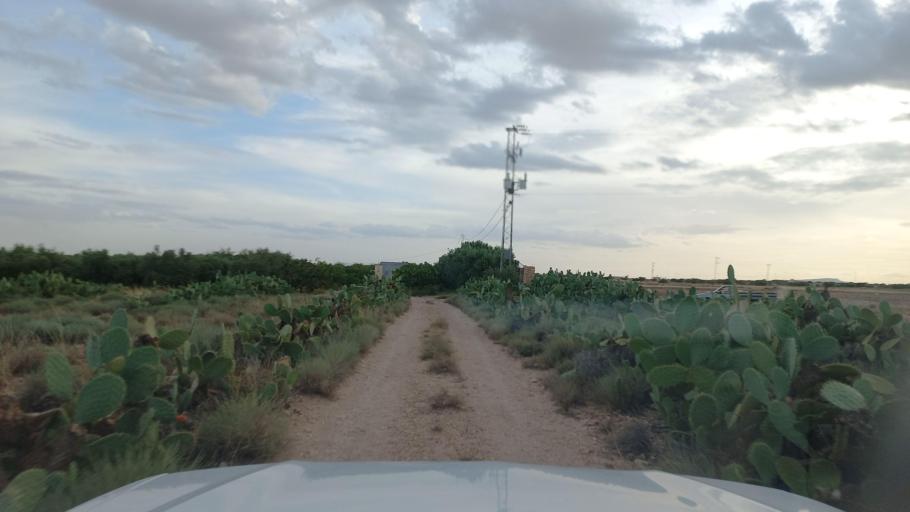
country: TN
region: Al Qasrayn
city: Sbiba
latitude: 35.4403
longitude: 9.0874
